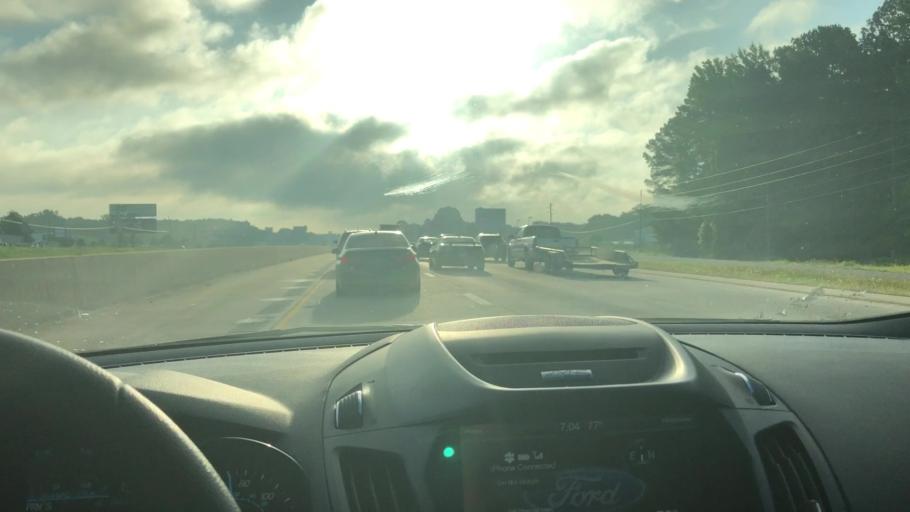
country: US
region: Arkansas
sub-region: Pulaski County
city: Alexander
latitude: 34.6352
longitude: -92.4585
